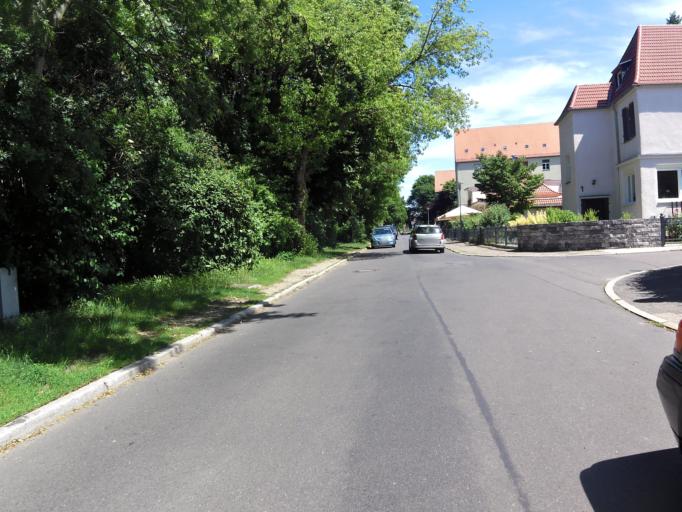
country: DE
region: Saxony
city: Markkleeberg
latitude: 51.3053
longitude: 12.3948
